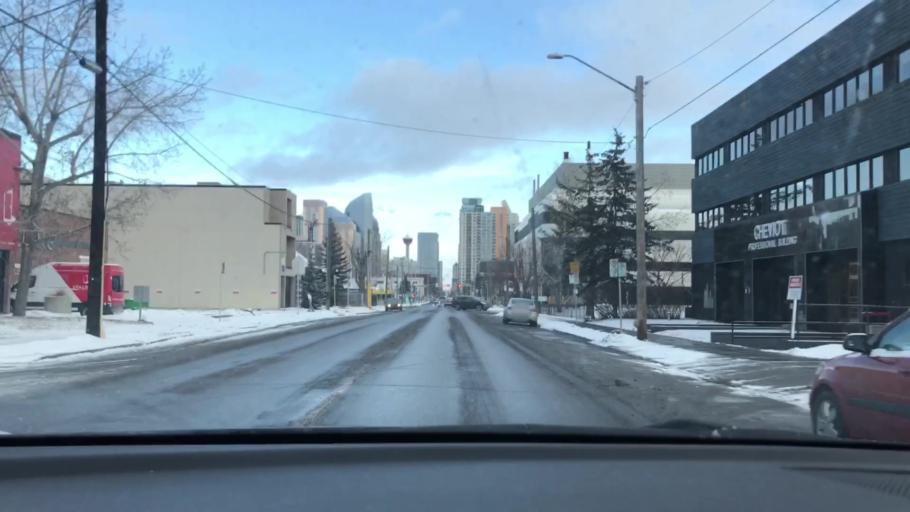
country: CA
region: Alberta
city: Calgary
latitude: 51.0443
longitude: -114.0981
